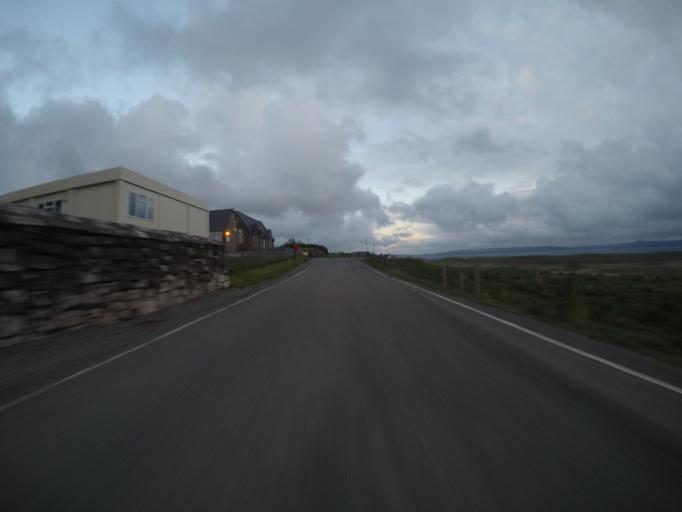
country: GB
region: Scotland
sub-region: Highland
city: Portree
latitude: 57.6361
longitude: -6.3764
